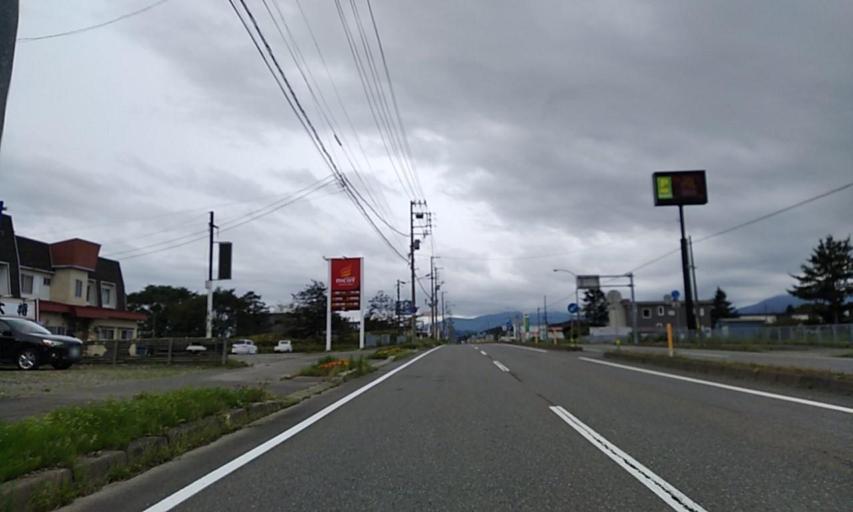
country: JP
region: Hokkaido
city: Obihiro
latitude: 42.3073
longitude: 143.3192
